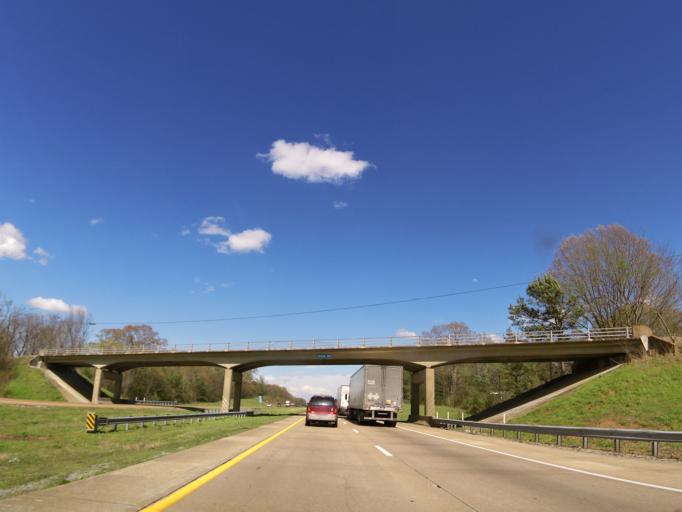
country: US
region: Tennessee
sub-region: Madison County
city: Jackson
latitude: 35.6895
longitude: -88.7141
